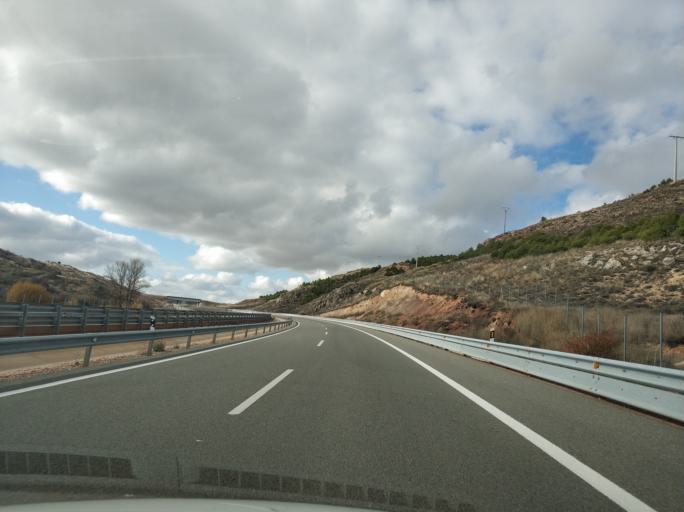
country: ES
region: Castille and Leon
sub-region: Provincia de Soria
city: Medinaceli
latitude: 41.1933
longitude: -2.4365
